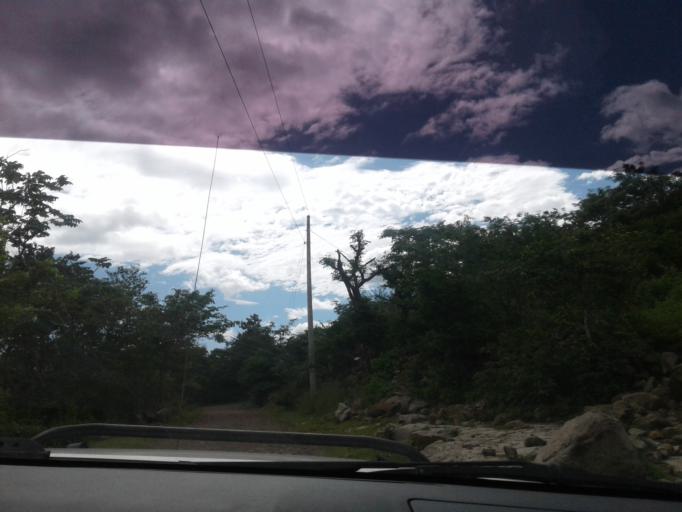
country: NI
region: Leon
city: Santa Rosa del Penon
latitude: 12.8606
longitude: -86.2318
